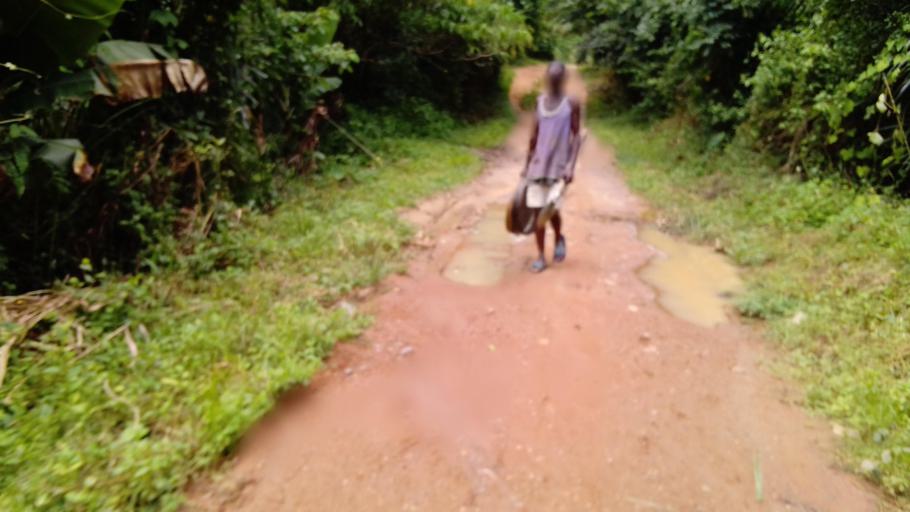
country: SL
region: Eastern Province
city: Koidu
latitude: 8.6586
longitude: -10.9346
